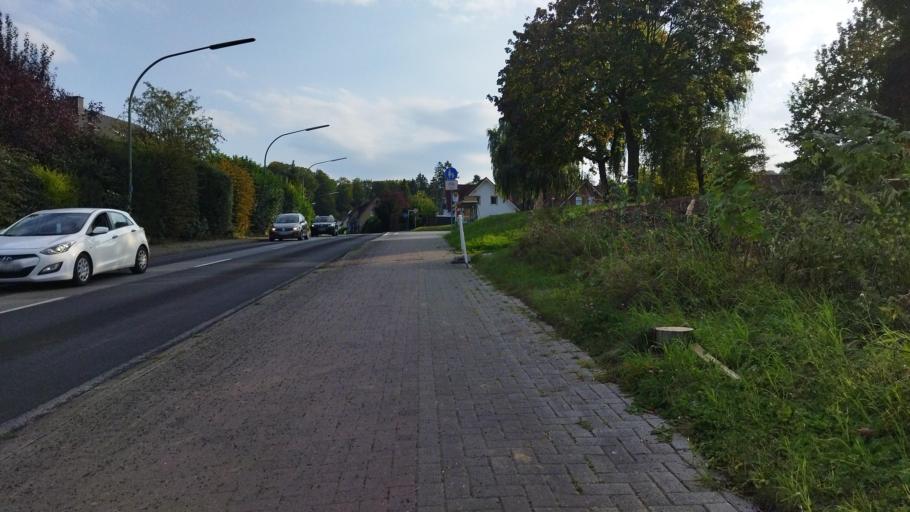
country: DE
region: Lower Saxony
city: Hagen
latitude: 52.2179
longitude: 8.0037
